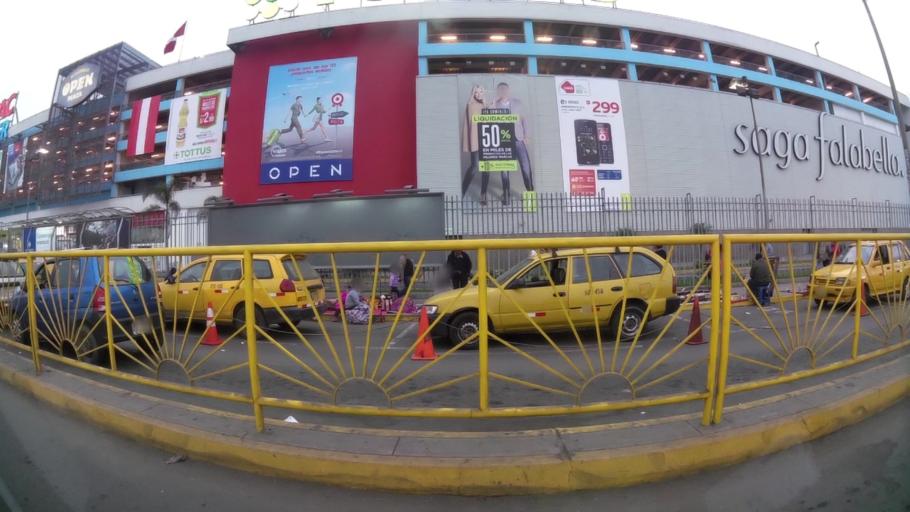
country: PE
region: Lima
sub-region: Lima
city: Surco
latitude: -12.1472
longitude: -76.9820
